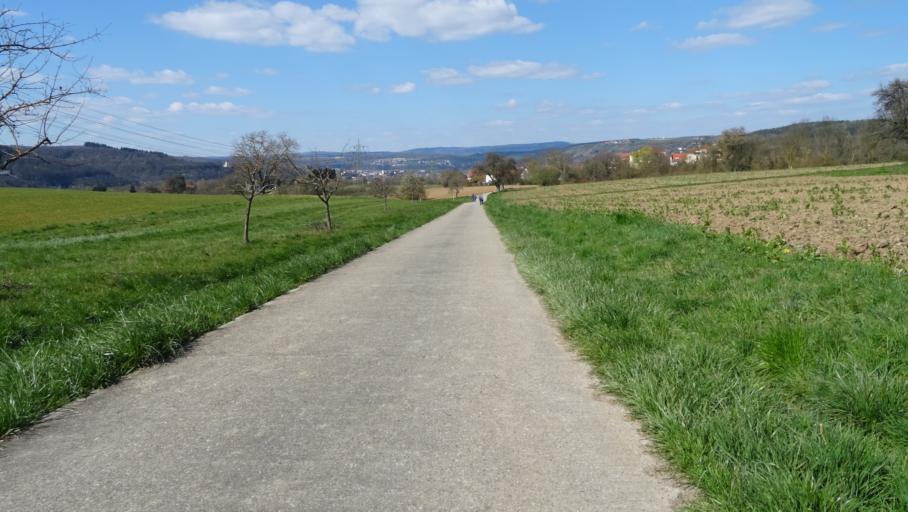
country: DE
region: Baden-Wuerttemberg
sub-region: Karlsruhe Region
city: Neckarzimmern
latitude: 49.3294
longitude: 9.1203
